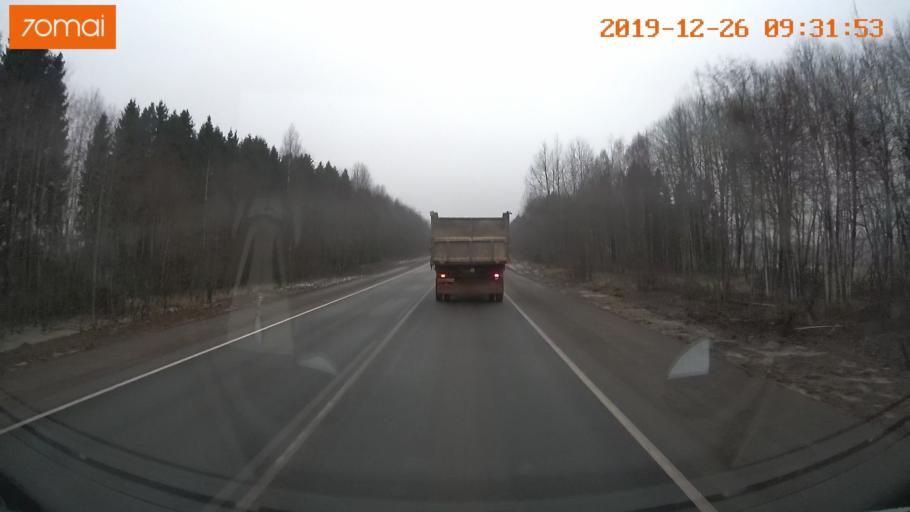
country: RU
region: Vologda
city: Gryazovets
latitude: 59.0729
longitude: 40.1230
